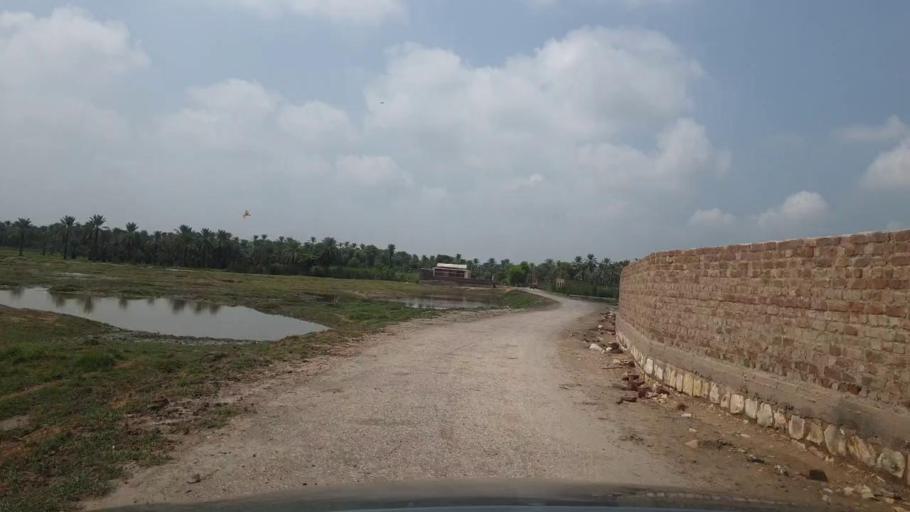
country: PK
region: Sindh
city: Pir jo Goth
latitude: 27.6237
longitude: 68.6789
